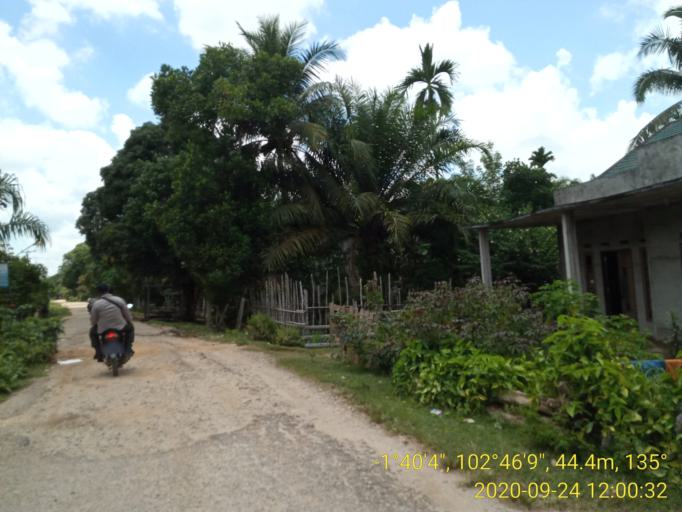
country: ID
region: Jambi
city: Sungaibengkal
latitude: -1.6680
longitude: 102.7692
